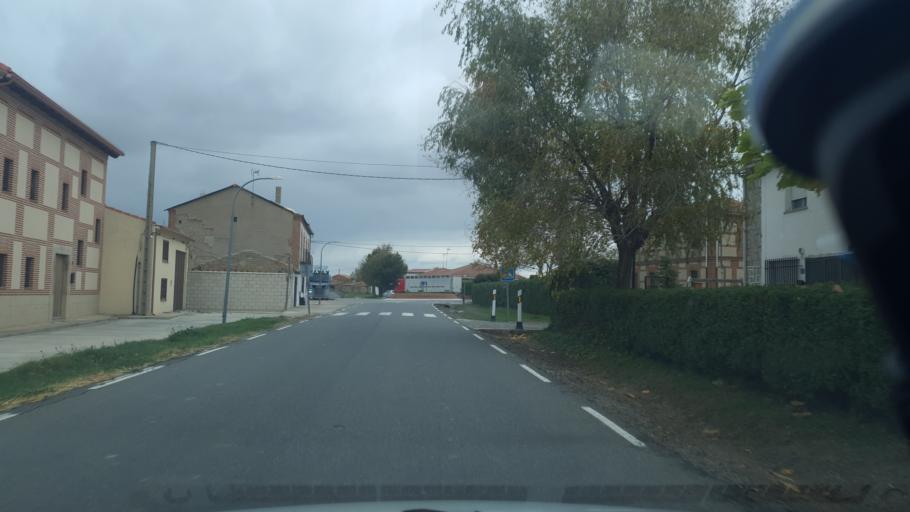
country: ES
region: Castille and Leon
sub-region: Provincia de Avila
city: Velayos
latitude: 40.8393
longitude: -4.6225
